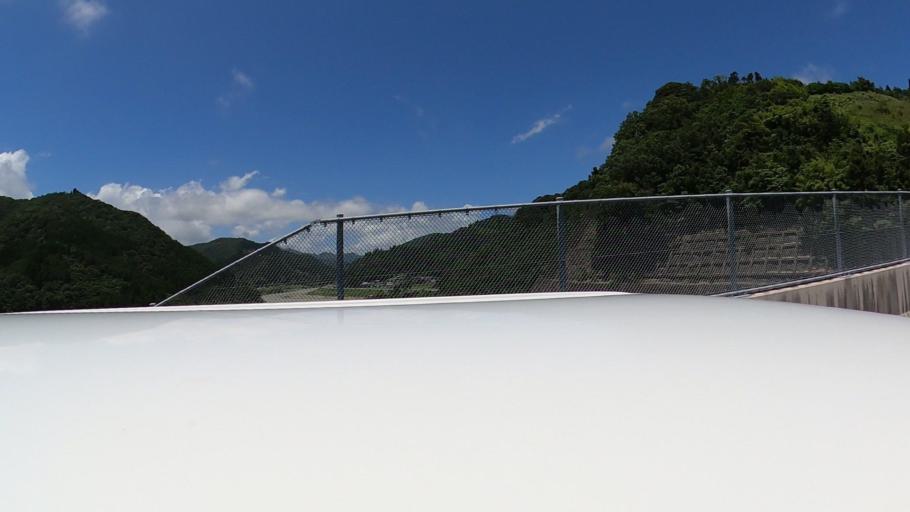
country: JP
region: Miyazaki
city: Takanabe
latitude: 32.3443
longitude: 131.5996
